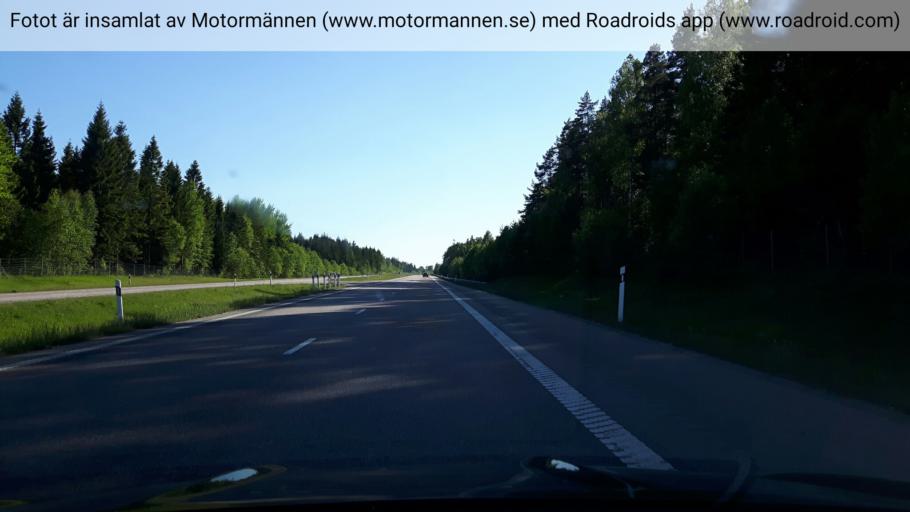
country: SE
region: Stockholm
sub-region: Norrtalje Kommun
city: Rimbo
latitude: 59.6796
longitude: 18.4098
